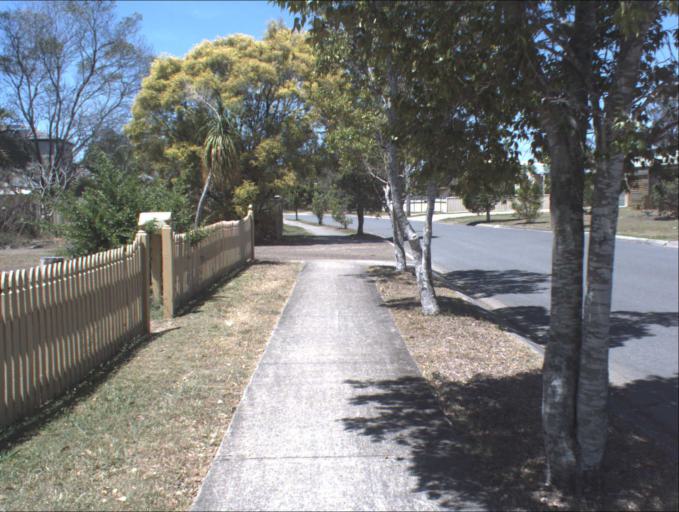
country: AU
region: Queensland
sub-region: Logan
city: Beenleigh
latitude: -27.6802
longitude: 153.1833
